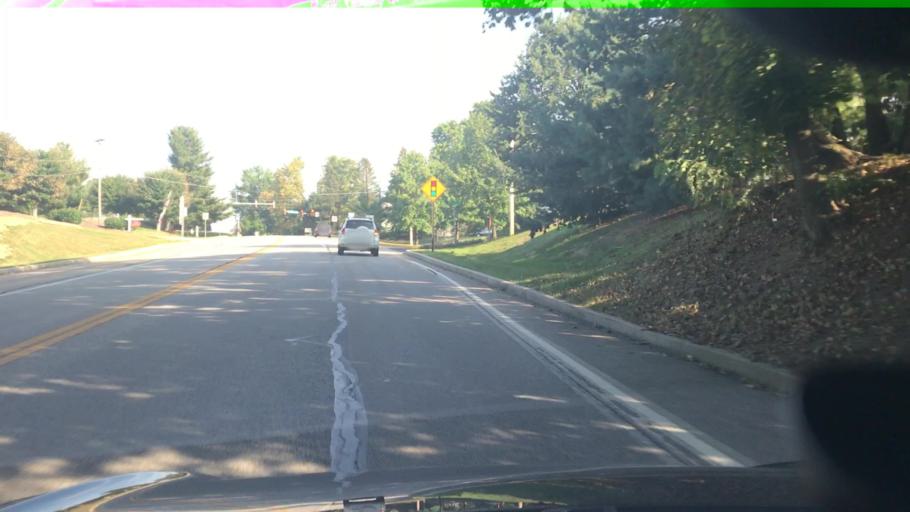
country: US
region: Pennsylvania
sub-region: Cumberland County
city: Shiremanstown
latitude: 40.2069
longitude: -76.9379
